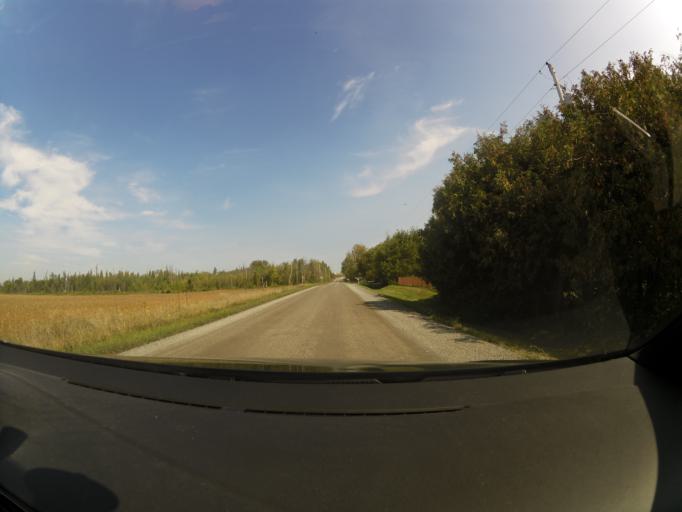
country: CA
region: Ontario
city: Arnprior
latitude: 45.3437
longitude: -76.2067
